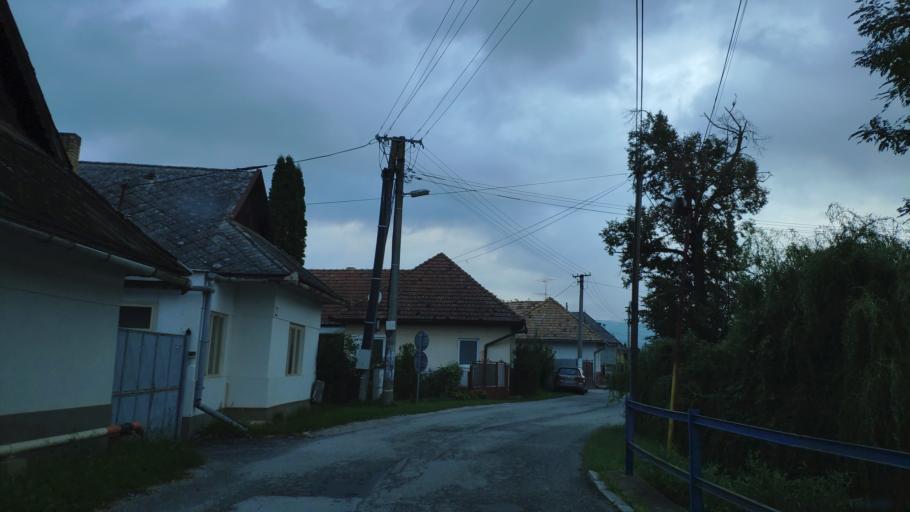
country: SK
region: Kosicky
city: Moldava nad Bodvou
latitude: 48.5808
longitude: 20.8875
